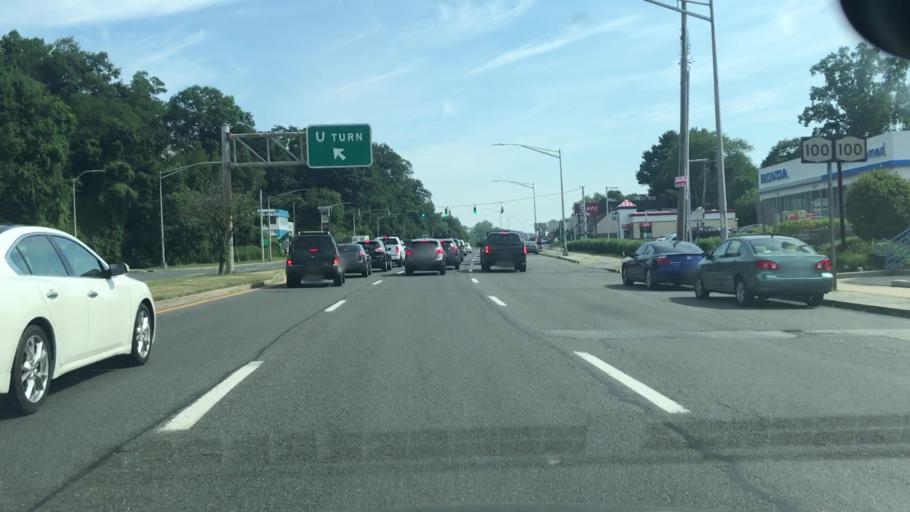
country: US
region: New York
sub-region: Westchester County
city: Tuckahoe
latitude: 40.9666
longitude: -73.8380
